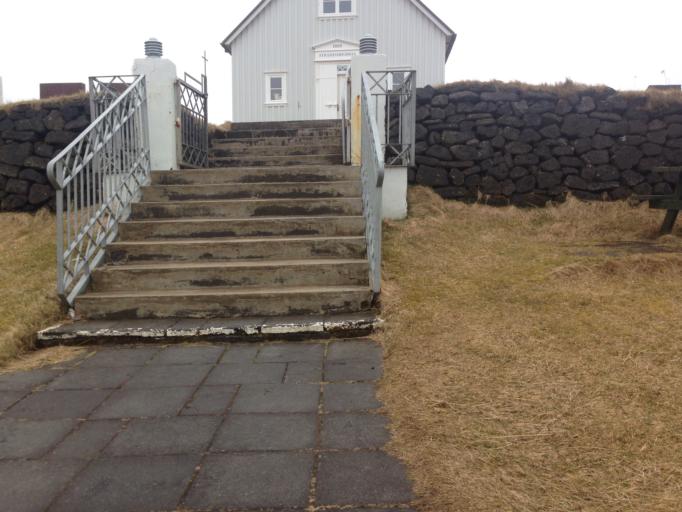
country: IS
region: South
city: THorlakshoefn
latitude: 63.8359
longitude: -21.7051
